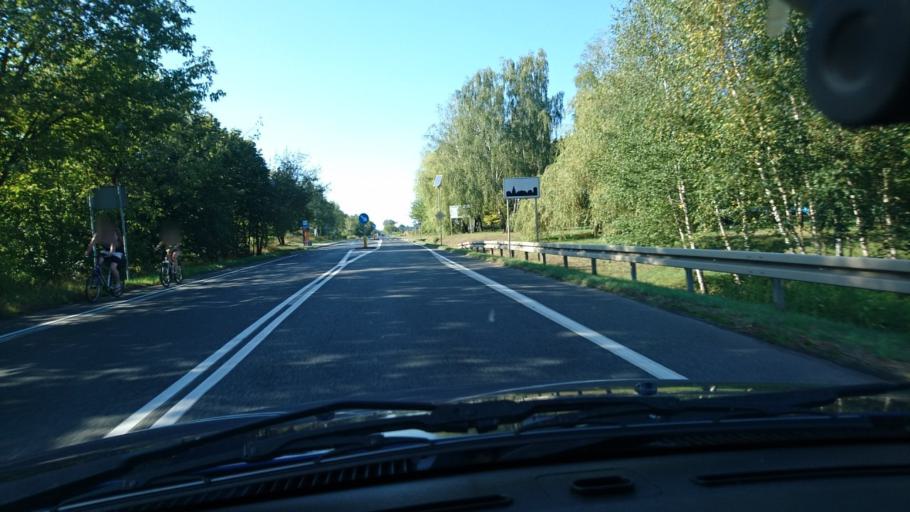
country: PL
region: Silesian Voivodeship
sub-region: Powiat gliwicki
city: Pyskowice
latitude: 50.3584
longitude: 18.6426
